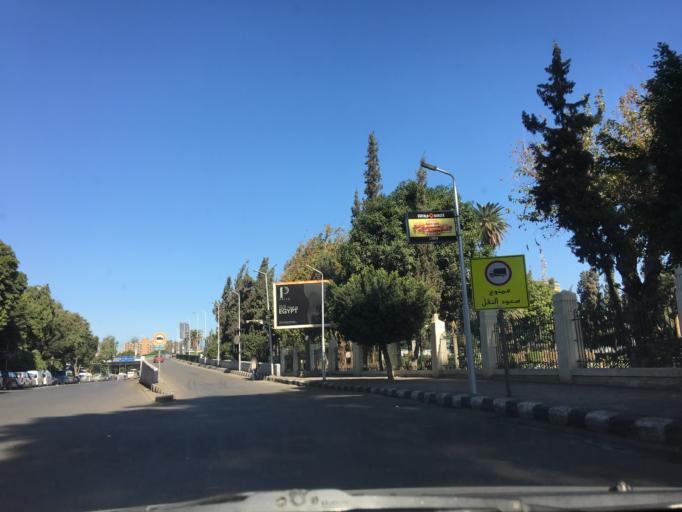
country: EG
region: Muhafazat al Qahirah
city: Cairo
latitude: 30.0467
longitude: 31.2270
